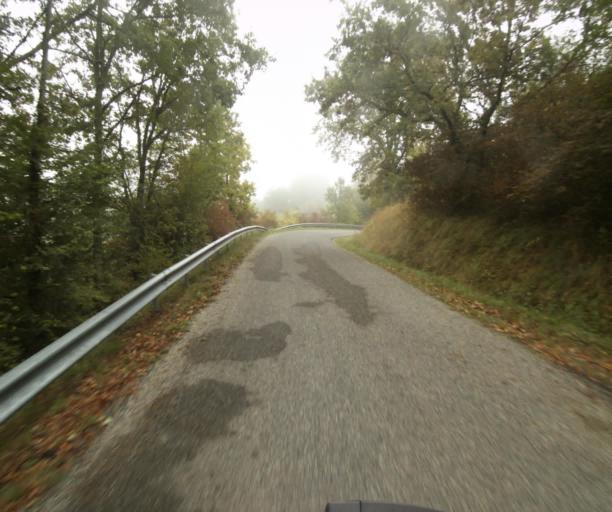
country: FR
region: Midi-Pyrenees
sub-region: Departement de la Haute-Garonne
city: Villemur-sur-Tarn
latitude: 43.8905
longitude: 1.4871
